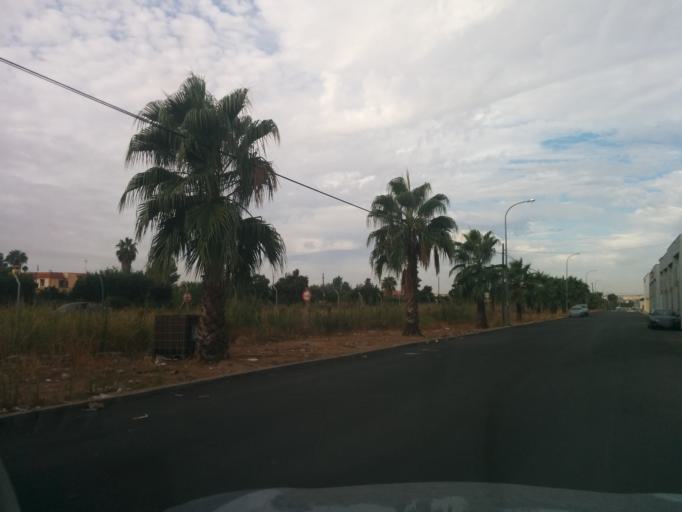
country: ES
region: Andalusia
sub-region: Provincia de Sevilla
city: Guillena
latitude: 37.5556
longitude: -6.0317
